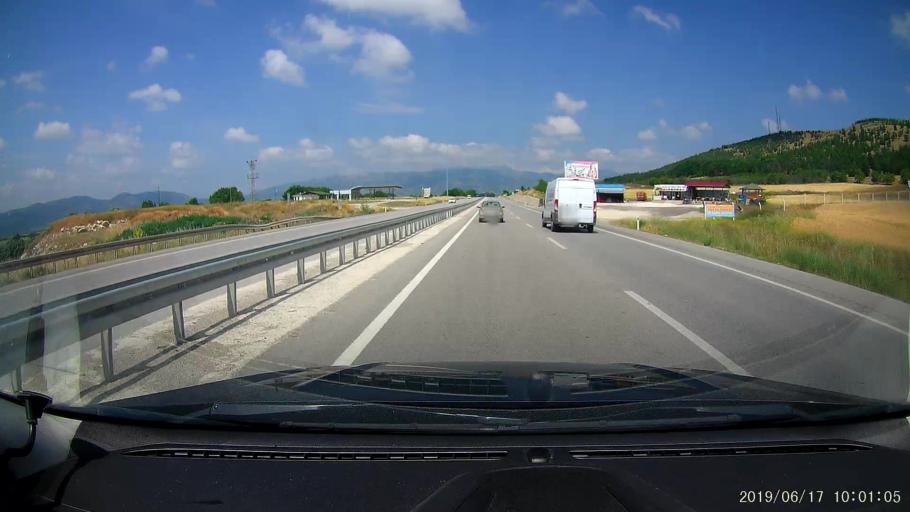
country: TR
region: Amasya
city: Gumushacikoy
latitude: 40.8665
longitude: 35.2735
